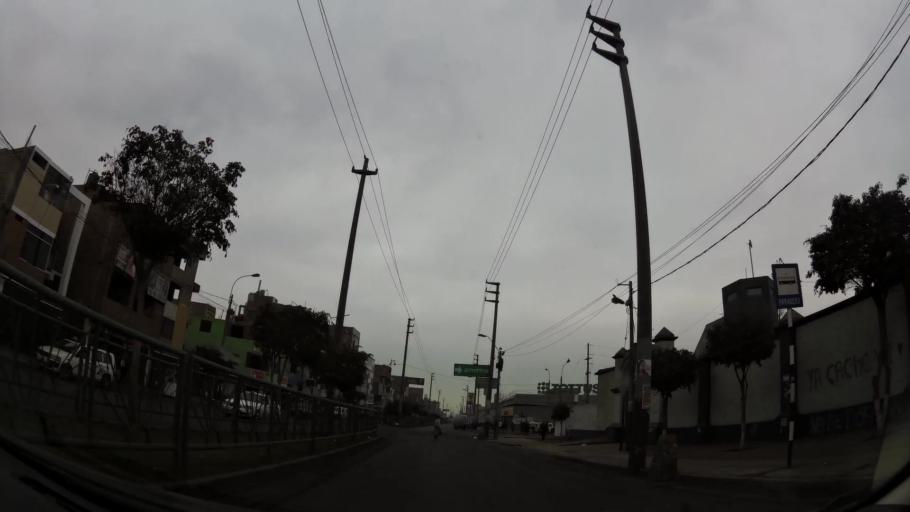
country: PE
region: Lima
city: Lima
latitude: -12.0405
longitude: -76.9988
